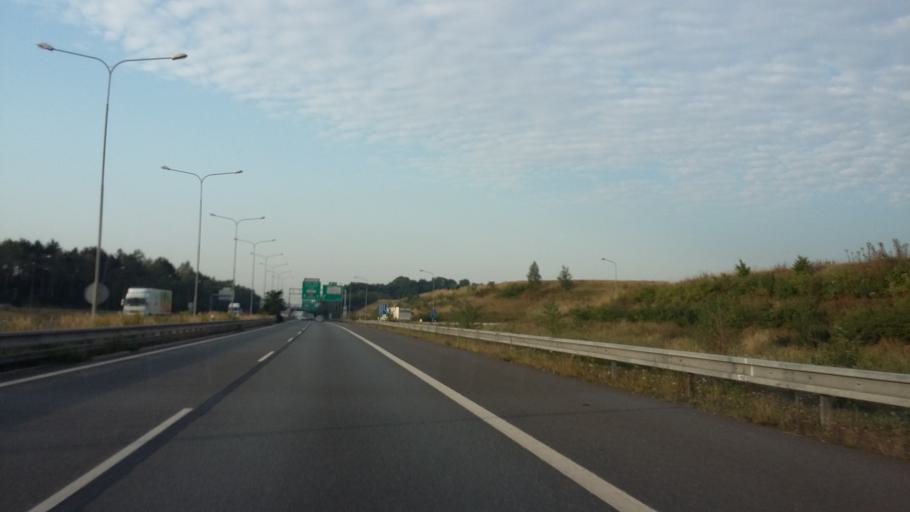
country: CZ
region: Praha
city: Cerny Most
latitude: 50.1179
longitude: 14.5886
